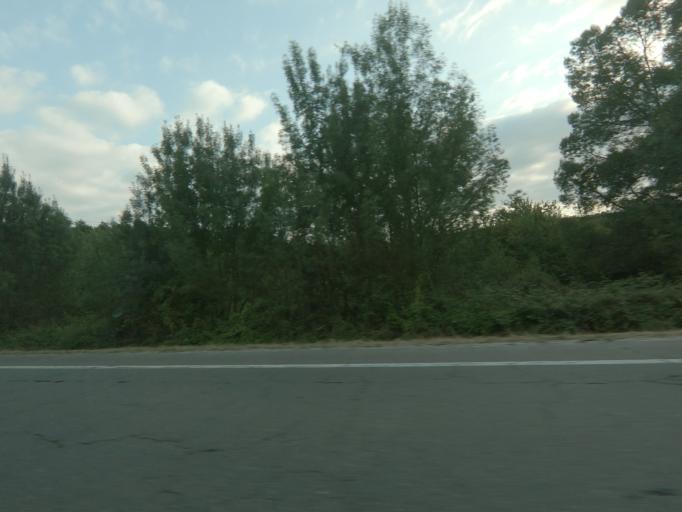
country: ES
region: Galicia
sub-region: Provincia de Ourense
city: Taboadela
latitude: 42.2801
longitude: -7.8376
